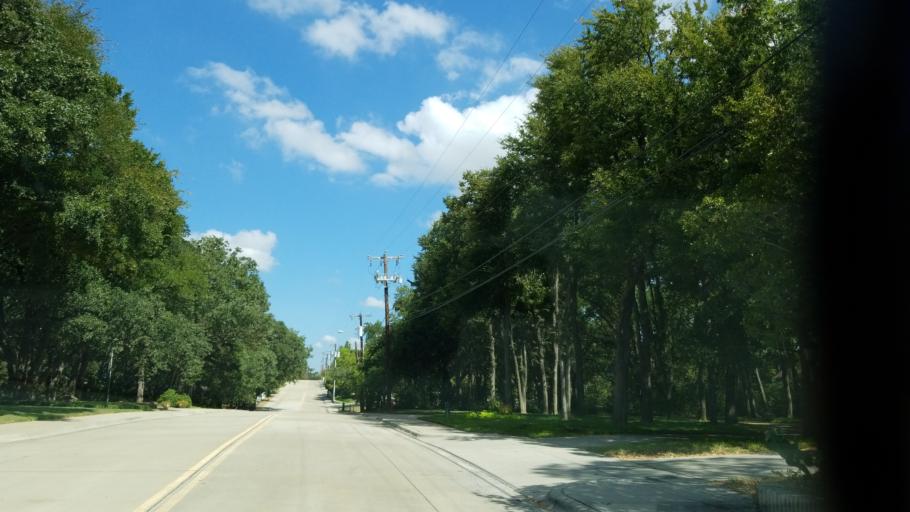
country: US
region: Texas
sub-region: Tarrant County
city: Euless
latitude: 32.8324
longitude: -97.0794
